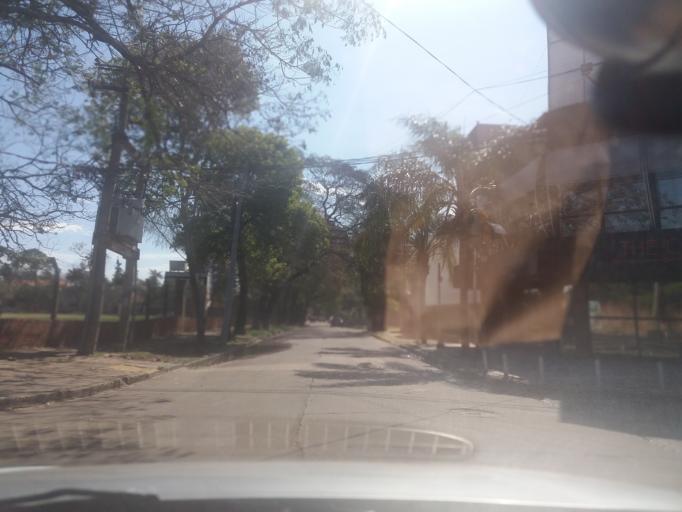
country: AR
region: Corrientes
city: Corrientes
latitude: -27.4699
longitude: -58.8509
